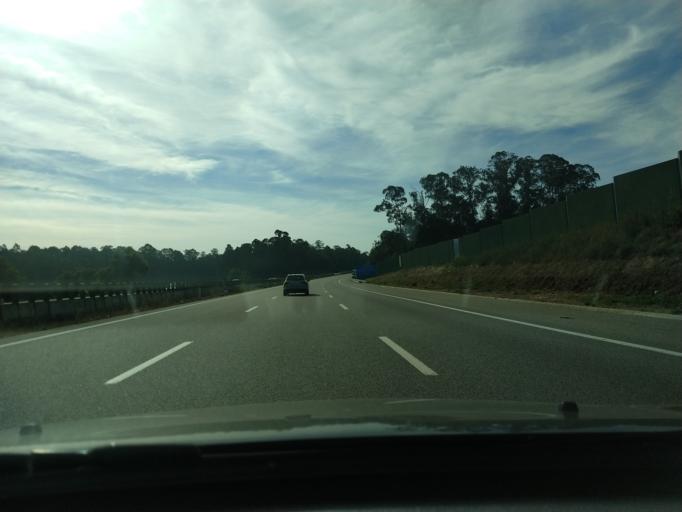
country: PT
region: Aveiro
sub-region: Ovar
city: Valega
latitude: 40.8431
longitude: -8.5563
